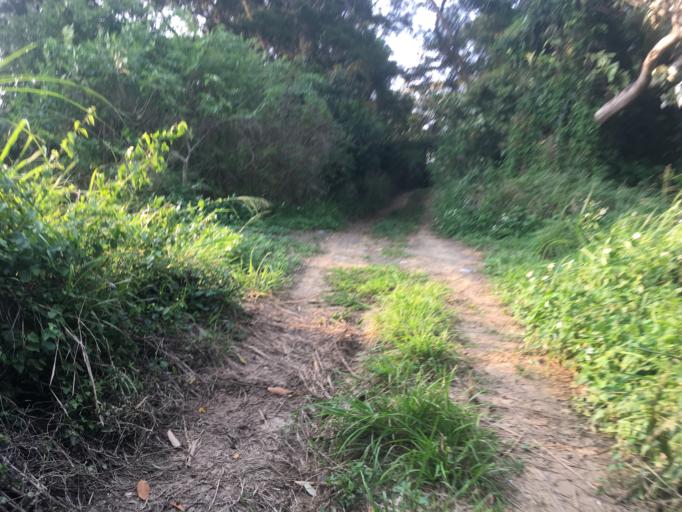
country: TW
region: Taiwan
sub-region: Hsinchu
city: Hsinchu
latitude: 24.7601
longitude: 120.9676
